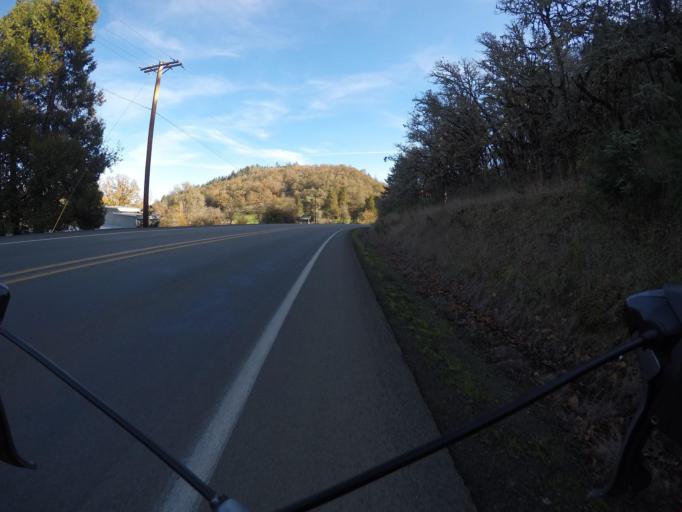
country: US
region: Oregon
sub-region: Douglas County
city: Winston
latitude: 43.1875
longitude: -123.4563
